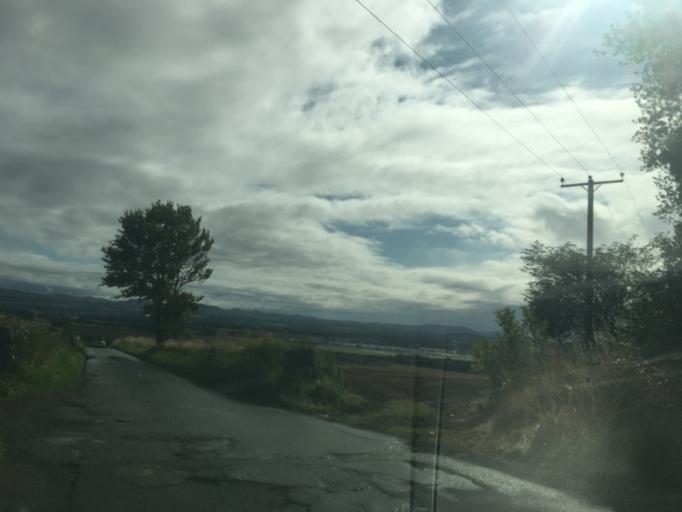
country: GB
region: Scotland
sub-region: Edinburgh
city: Queensferry
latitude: 55.9711
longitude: -3.3526
